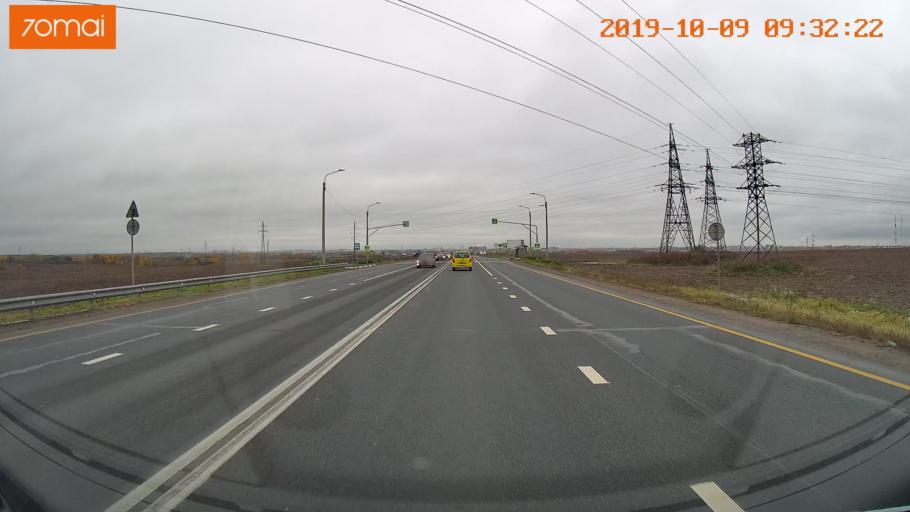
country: RU
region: Vologda
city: Vologda
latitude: 59.1580
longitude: 39.9292
